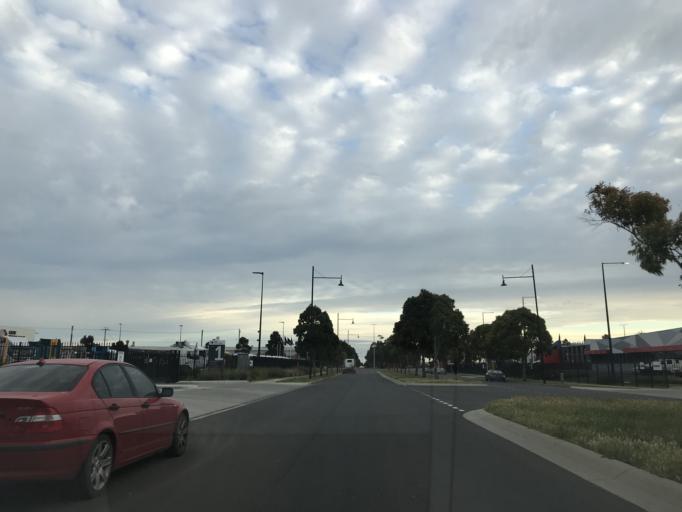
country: AU
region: Victoria
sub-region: Wyndham
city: Truganina
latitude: -37.8099
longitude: 144.7662
